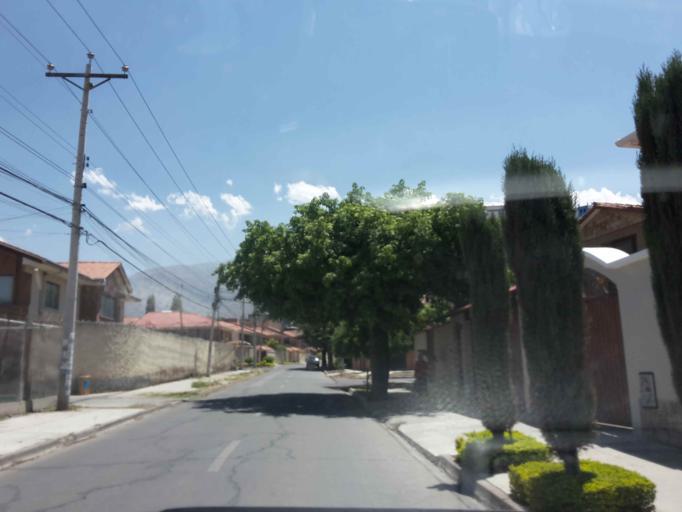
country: BO
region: Cochabamba
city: Cochabamba
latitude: -17.3732
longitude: -66.1845
